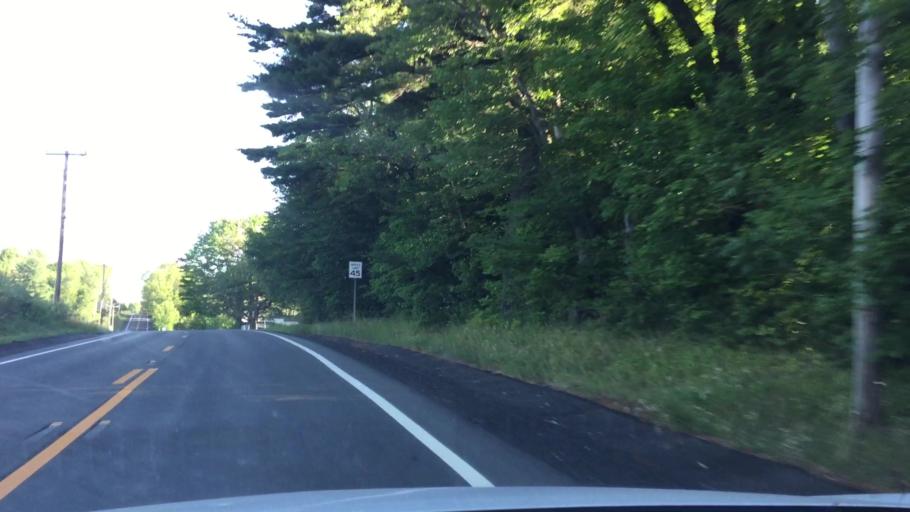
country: US
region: Massachusetts
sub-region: Berkshire County
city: Becket
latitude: 42.2732
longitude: -73.0550
